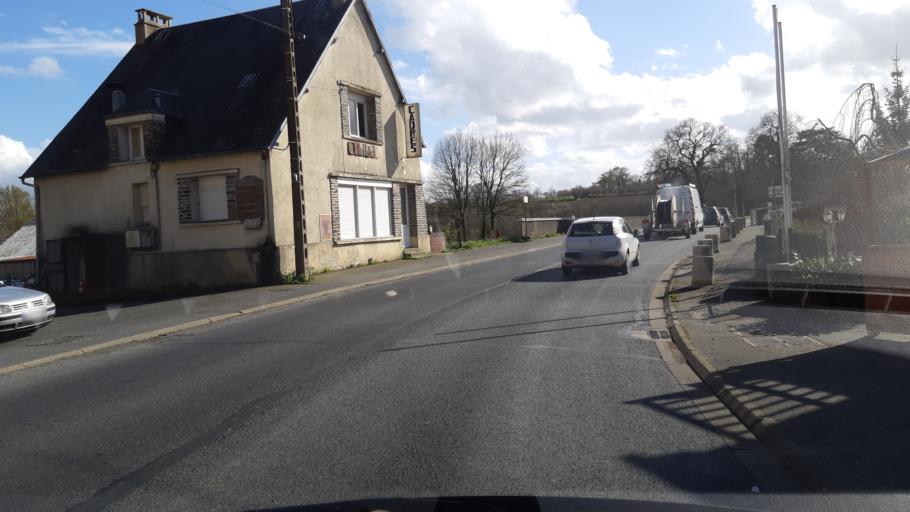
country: FR
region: Lower Normandy
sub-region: Departement de la Manche
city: Agneaux
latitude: 49.0925
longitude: -1.1171
